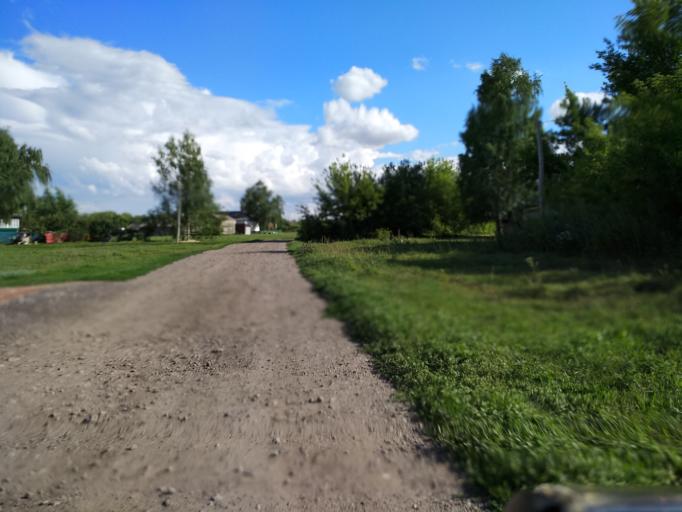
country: RU
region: Lipetsk
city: Dobrinka
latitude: 52.0308
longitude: 40.5626
